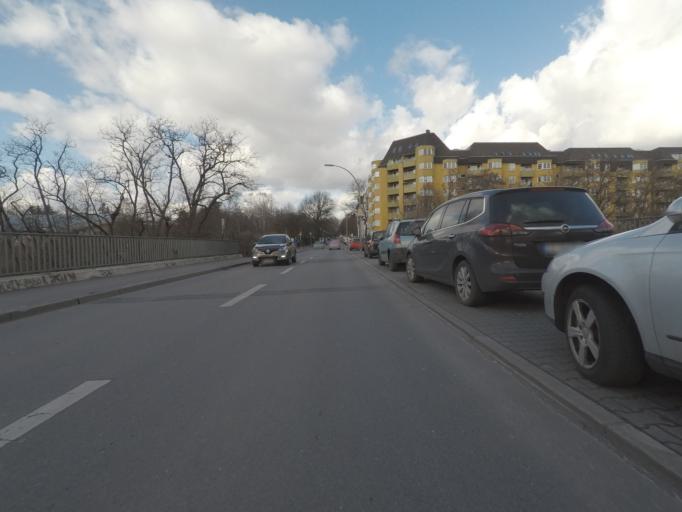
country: DE
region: Berlin
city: Tempelhof Bezirk
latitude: 52.4661
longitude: 13.4213
